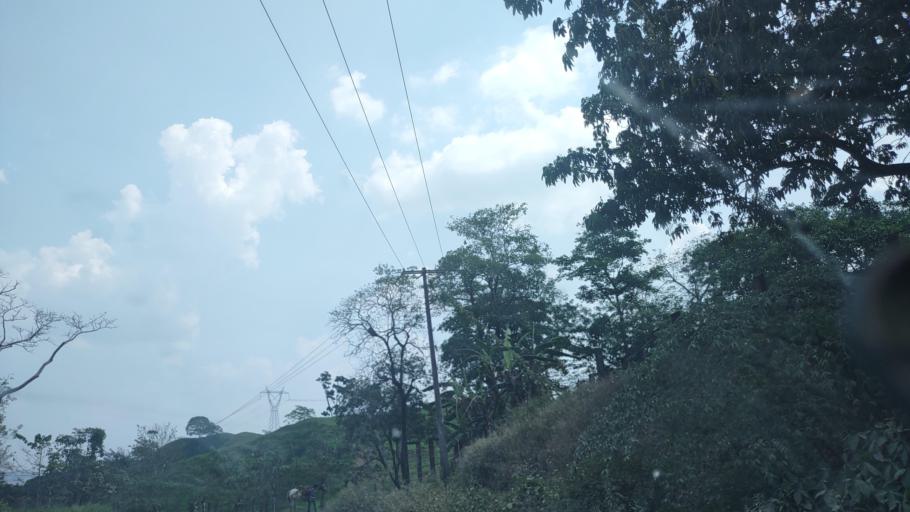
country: MX
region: Tabasco
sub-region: Huimanguillo
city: Francisco Rueda
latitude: 17.5968
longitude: -93.8998
